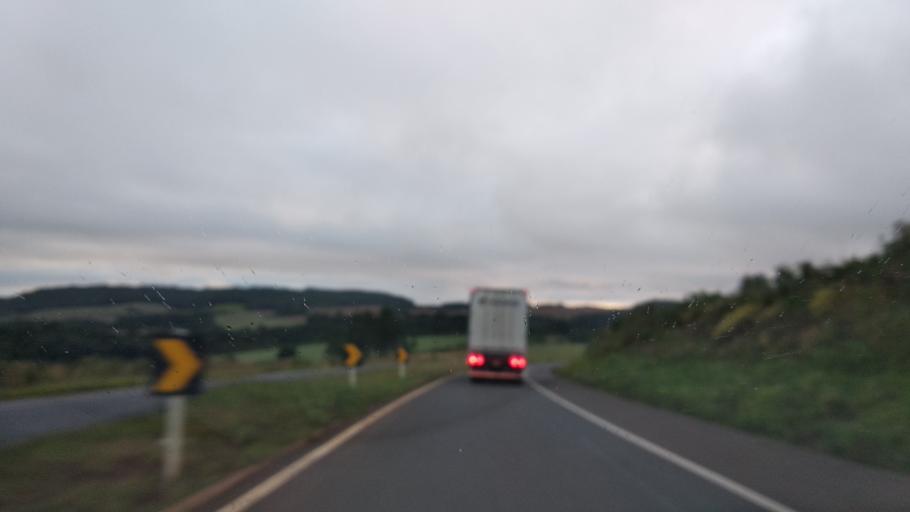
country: BR
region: Santa Catarina
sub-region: Campos Novos
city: Campos Novos
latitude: -27.3742
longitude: -51.0709
